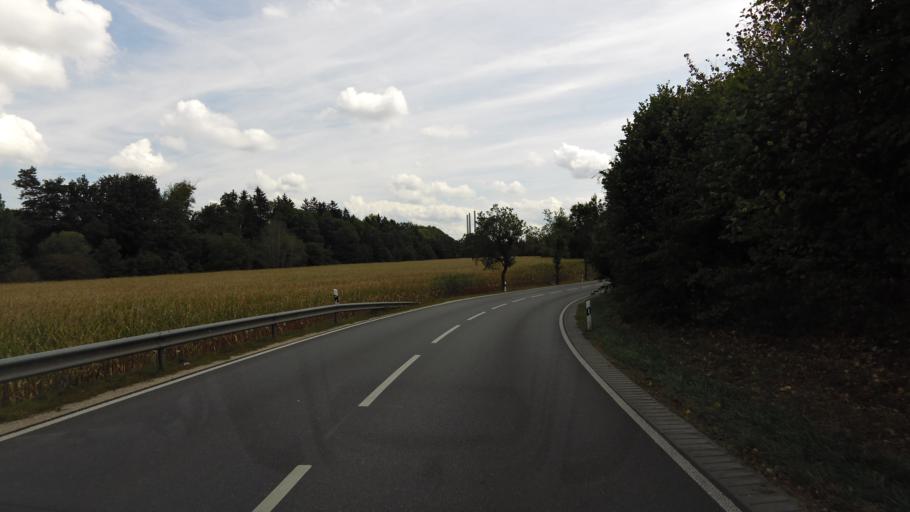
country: DE
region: Bavaria
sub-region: Upper Bavaria
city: Unterneukirchen
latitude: 48.1520
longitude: 12.6130
